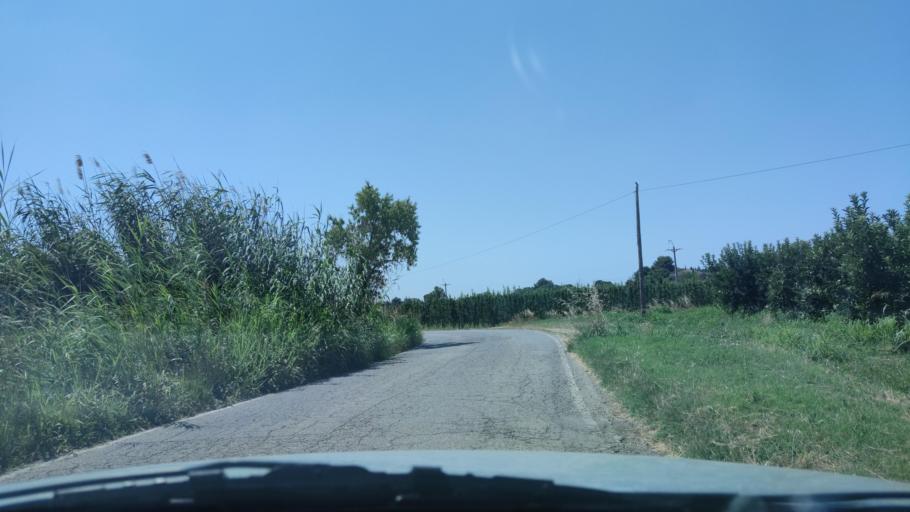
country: ES
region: Catalonia
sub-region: Provincia de Lleida
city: Torrefarrera
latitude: 41.6501
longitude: 0.5989
